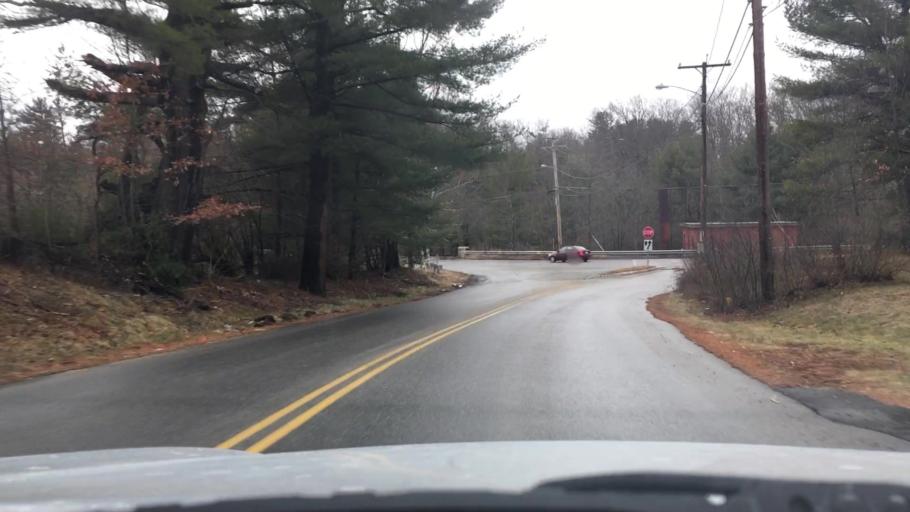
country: US
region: Massachusetts
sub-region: Franklin County
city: Orange
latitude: 42.5698
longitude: -72.2711
